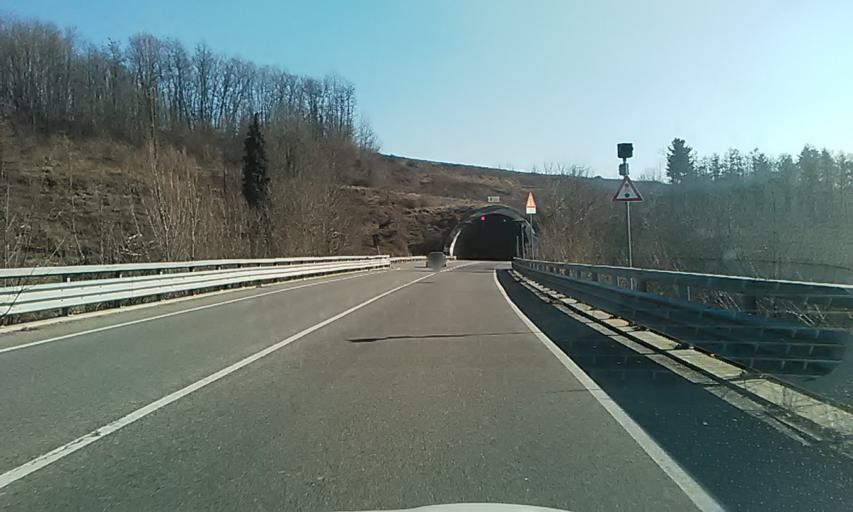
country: IT
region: Piedmont
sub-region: Provincia di Novara
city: Prato Sesia
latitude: 45.6560
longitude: 8.3812
